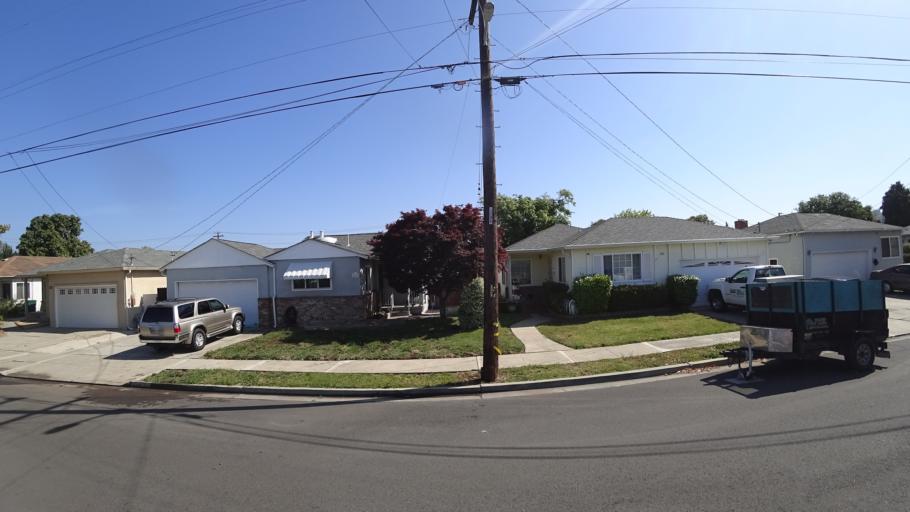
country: US
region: California
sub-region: Alameda County
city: Hayward
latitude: 37.6583
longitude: -122.0829
